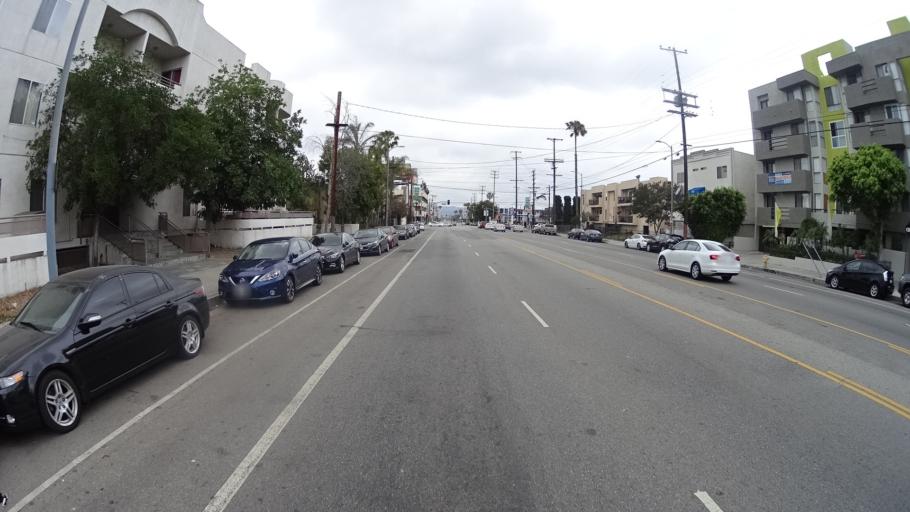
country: US
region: California
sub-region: Los Angeles County
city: North Hollywood
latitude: 34.1951
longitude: -118.3965
